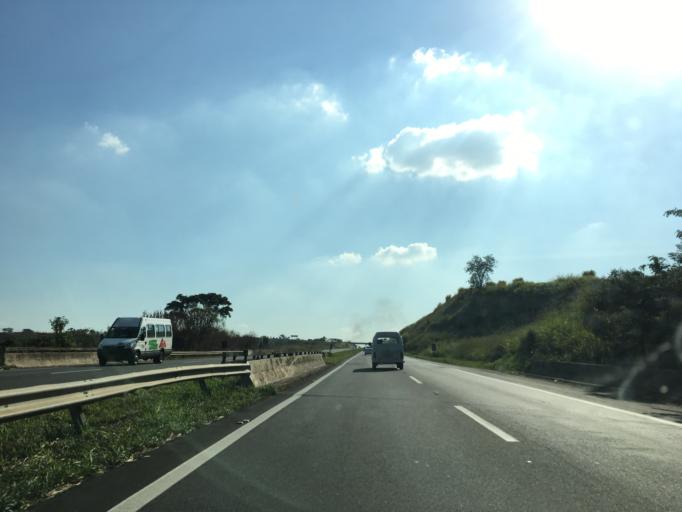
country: BR
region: Sao Paulo
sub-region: Santa Barbara D'Oeste
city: Santa Barbara d'Oeste
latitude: -22.7506
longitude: -47.4957
